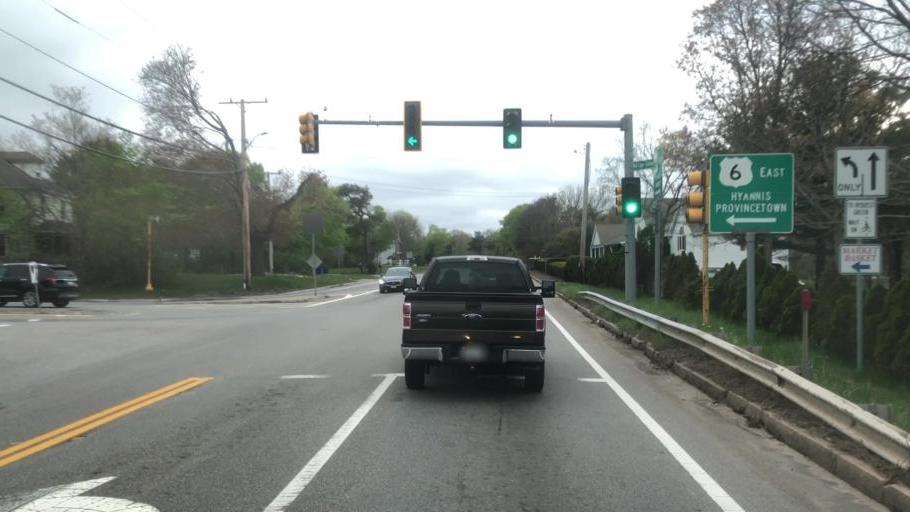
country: US
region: Massachusetts
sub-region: Barnstable County
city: Sagamore
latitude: 41.7744
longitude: -70.5473
